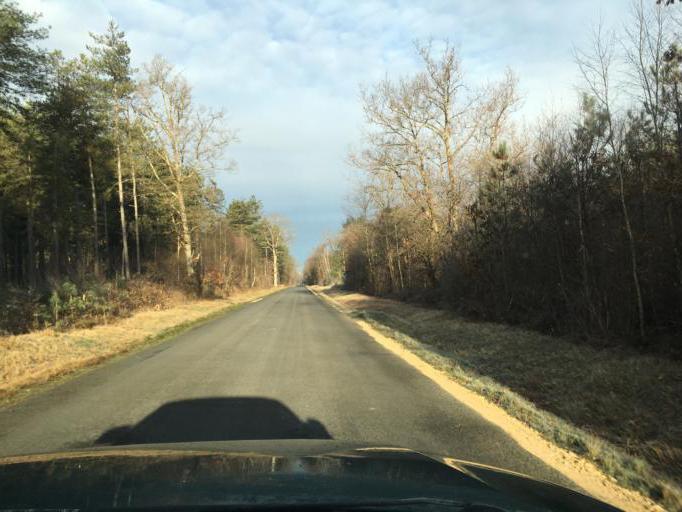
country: FR
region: Centre
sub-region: Departement du Loiret
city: Saint-Hilaire-Saint-Mesmin
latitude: 47.8084
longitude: 1.8150
